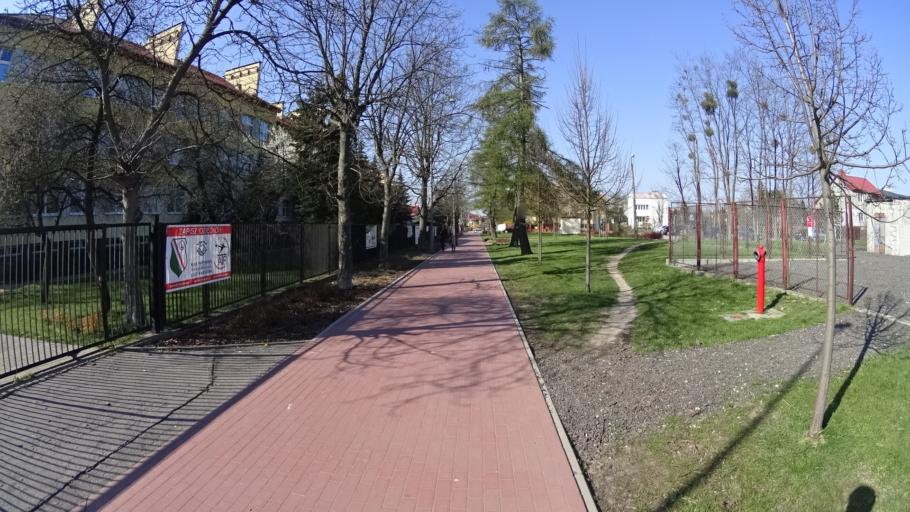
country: PL
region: Masovian Voivodeship
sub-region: Powiat warszawski zachodni
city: Babice
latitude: 52.2534
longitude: 20.8415
